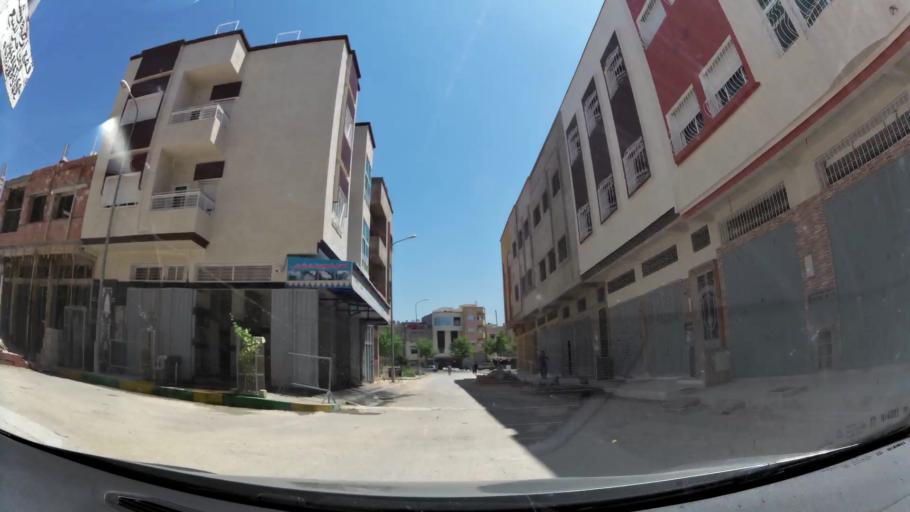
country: MA
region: Fes-Boulemane
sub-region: Fes
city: Fes
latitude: 34.0192
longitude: -5.0508
